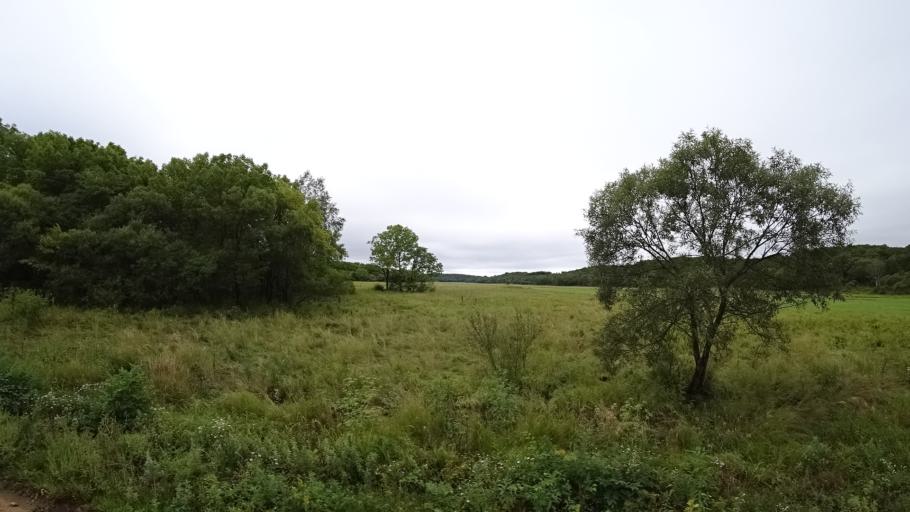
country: RU
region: Primorskiy
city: Rettikhovka
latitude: 44.0630
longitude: 132.6531
